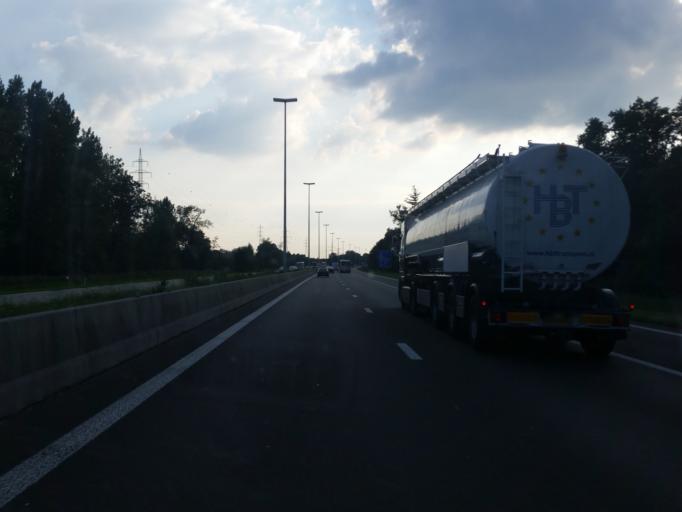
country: BE
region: Flanders
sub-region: Provincie Antwerpen
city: Zandhoven
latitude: 51.2211
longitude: 4.6440
